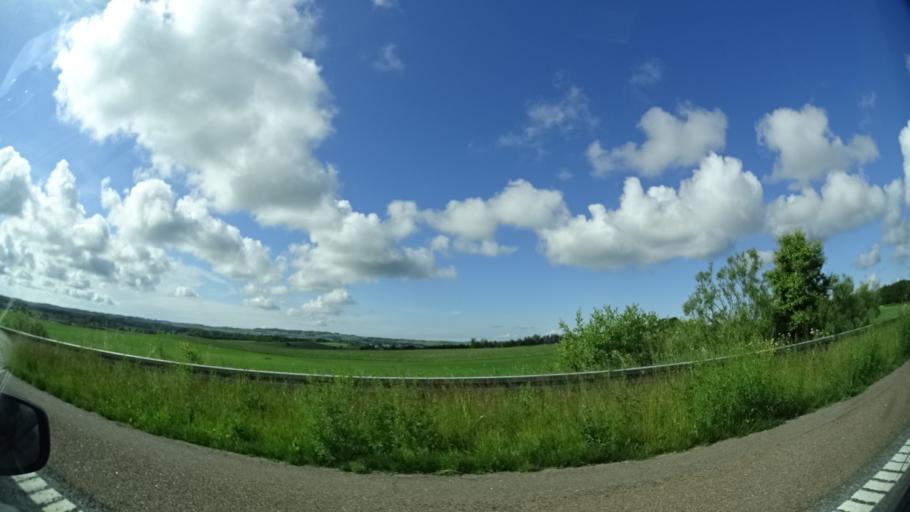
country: DK
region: Central Jutland
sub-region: Syddjurs Kommune
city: Ronde
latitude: 56.2959
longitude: 10.5224
